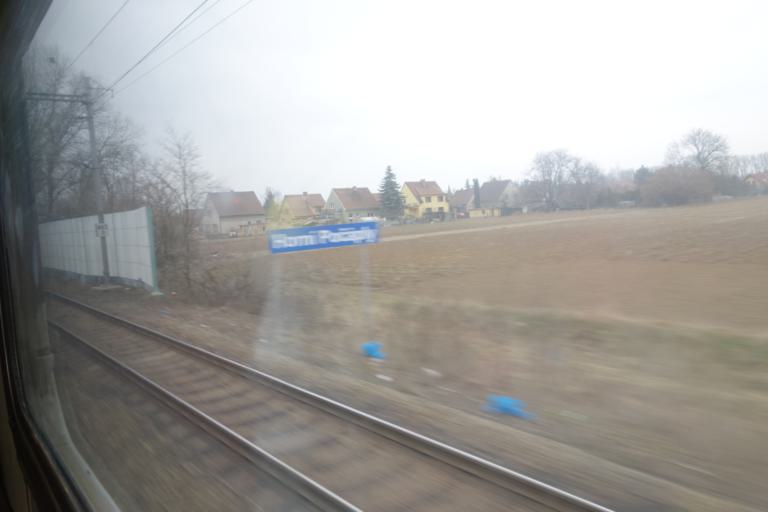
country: CZ
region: Central Bohemia
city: Horni Pocaply
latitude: 50.4196
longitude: 14.3930
